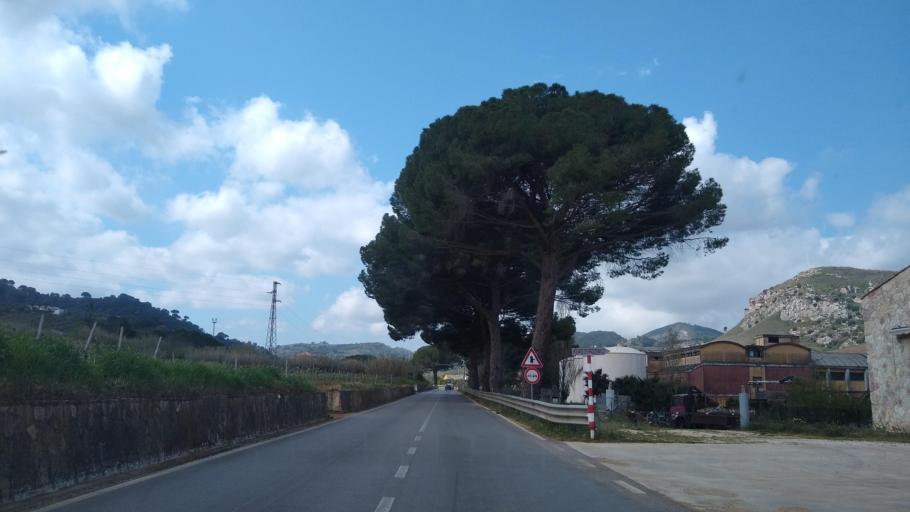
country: IT
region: Sicily
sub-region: Trapani
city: Calatafimi
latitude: 37.9423
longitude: 12.8582
